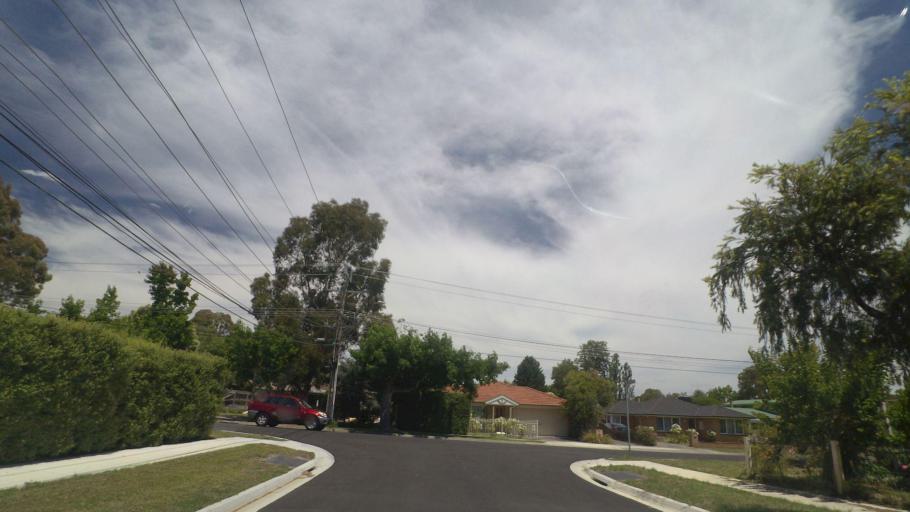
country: AU
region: Victoria
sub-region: Knox
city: Boronia
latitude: -37.8562
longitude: 145.2934
